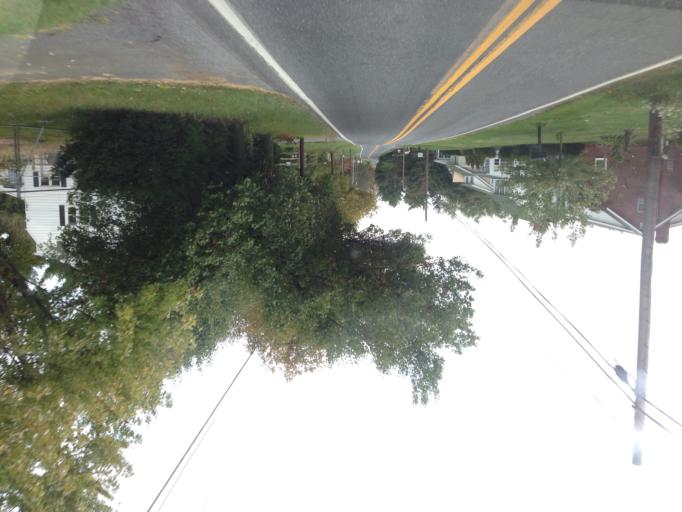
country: US
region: Maryland
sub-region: Carroll County
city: Mount Airy
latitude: 39.3367
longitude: -77.1542
